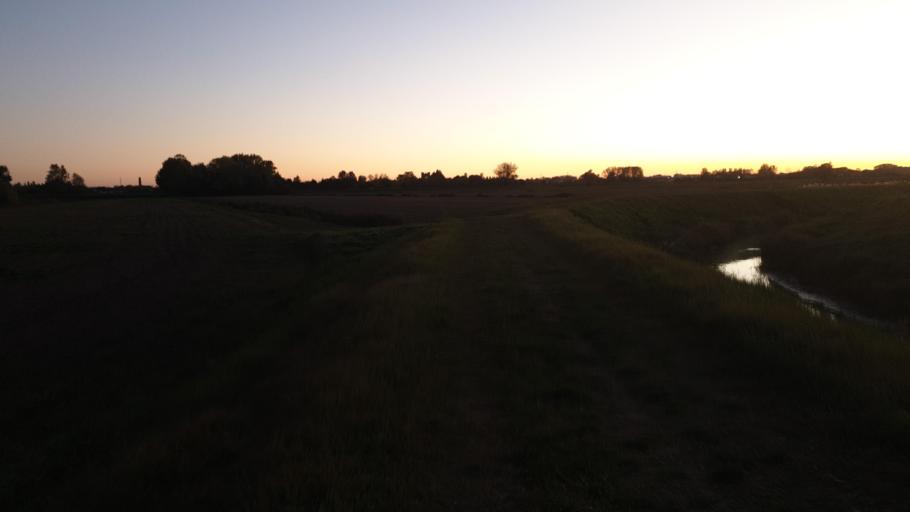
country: IT
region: Veneto
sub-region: Provincia di Venezia
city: Fiesso d'Artico
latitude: 45.4326
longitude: 12.0324
